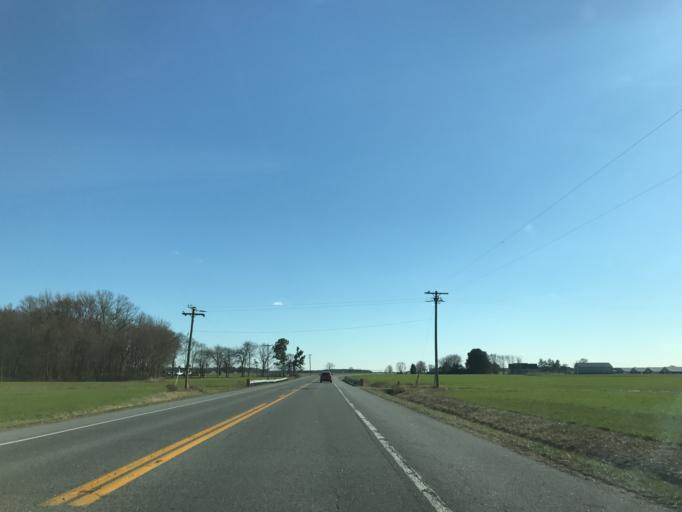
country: US
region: Maryland
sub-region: Caroline County
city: Greensboro
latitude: 39.1377
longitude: -75.8640
